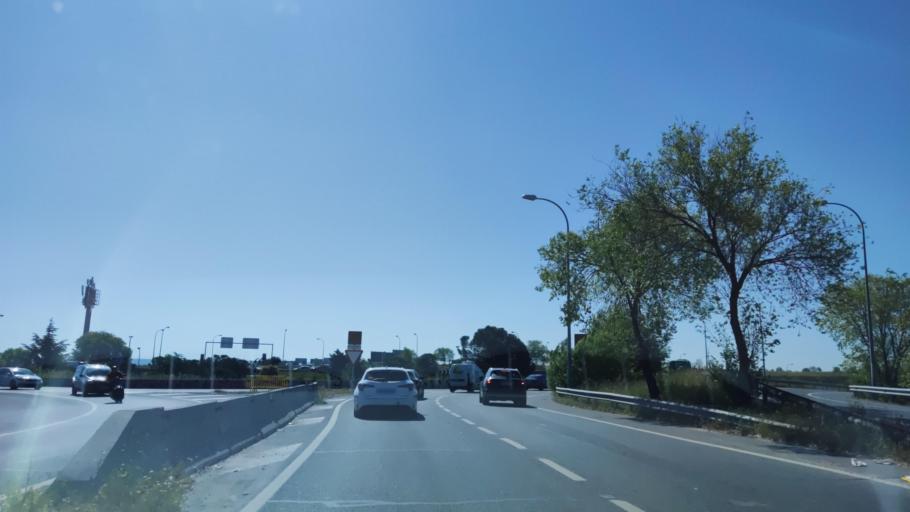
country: ES
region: Madrid
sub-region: Provincia de Madrid
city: San Blas
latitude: 40.4306
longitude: -3.5980
